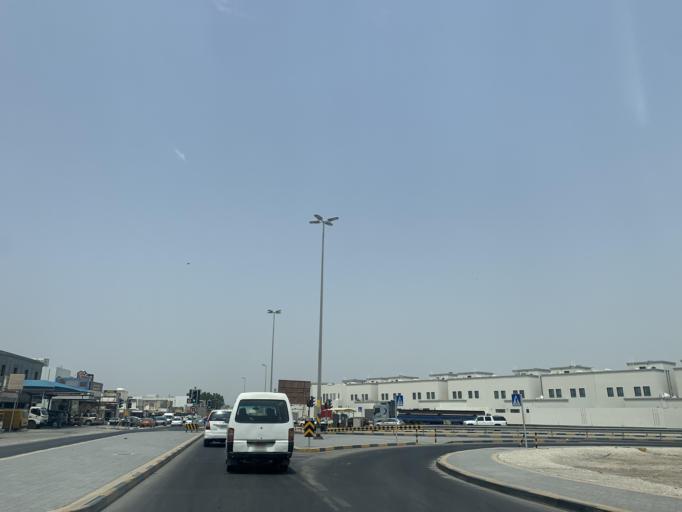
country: BH
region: Central Governorate
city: Madinat Hamad
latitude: 26.1332
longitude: 50.4812
